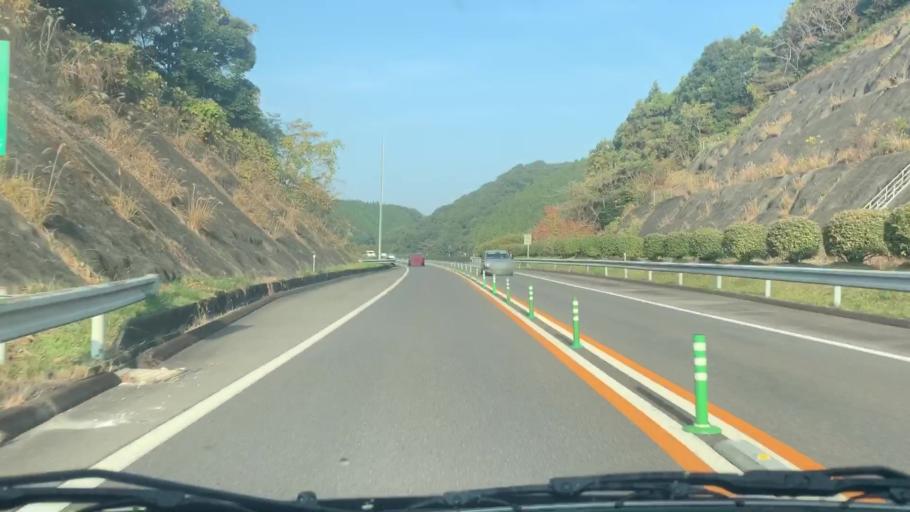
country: JP
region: Saga Prefecture
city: Ureshinomachi-shimojuku
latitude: 33.1459
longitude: 129.9507
